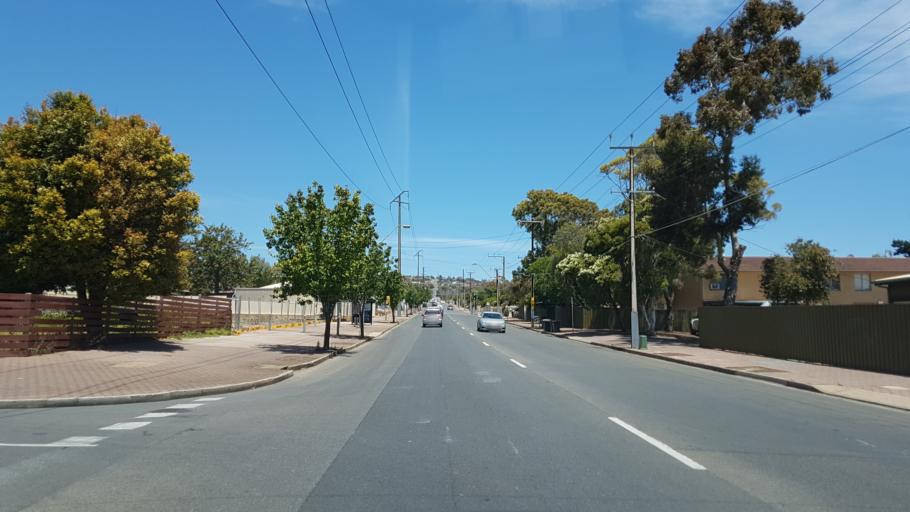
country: AU
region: South Australia
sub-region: Marion
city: Sturt
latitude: -35.0240
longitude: 138.5414
